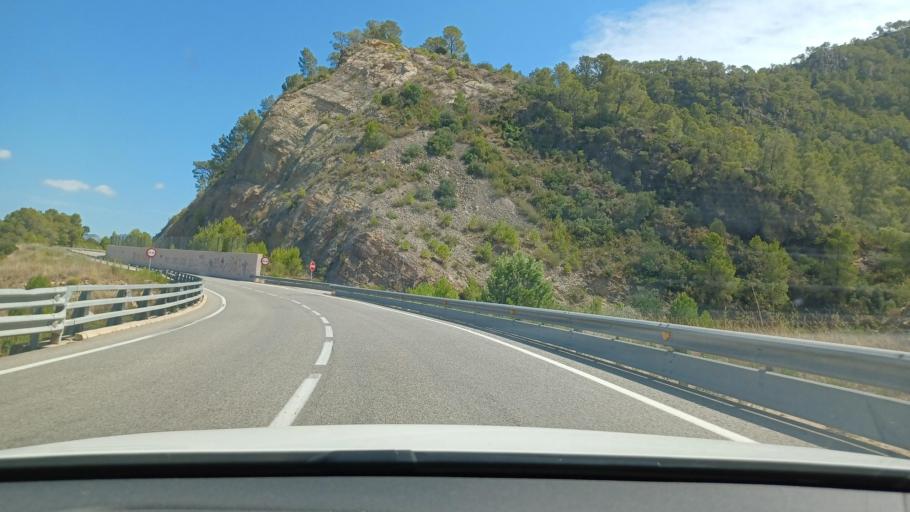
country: ES
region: Catalonia
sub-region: Provincia de Tarragona
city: Benifallet
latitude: 40.9510
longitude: 0.4516
